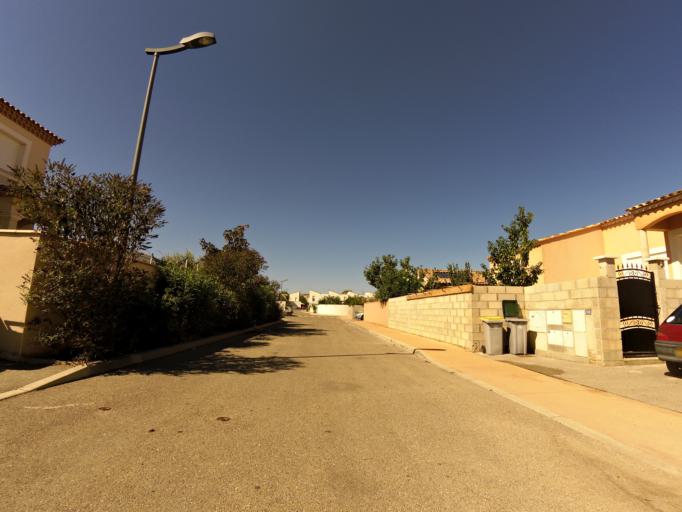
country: FR
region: Languedoc-Roussillon
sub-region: Departement du Gard
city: Vergeze
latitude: 43.7381
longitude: 4.2259
